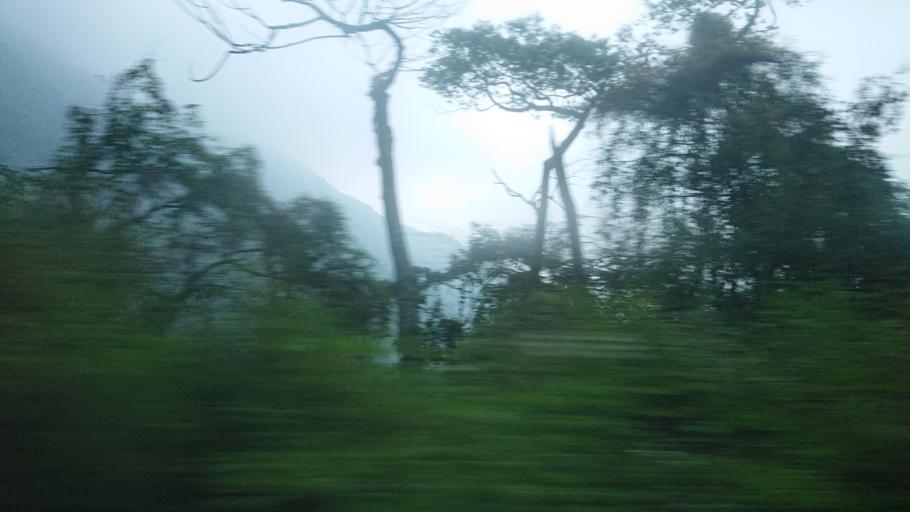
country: TW
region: Taiwan
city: Lugu
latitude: 23.5963
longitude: 120.7191
